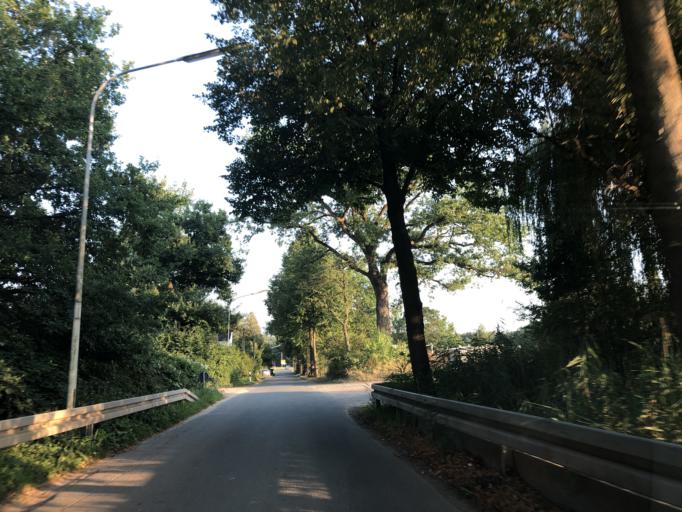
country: DE
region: Hesse
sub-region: Regierungsbezirk Darmstadt
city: Darmstadt
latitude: 49.8997
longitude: 8.6901
